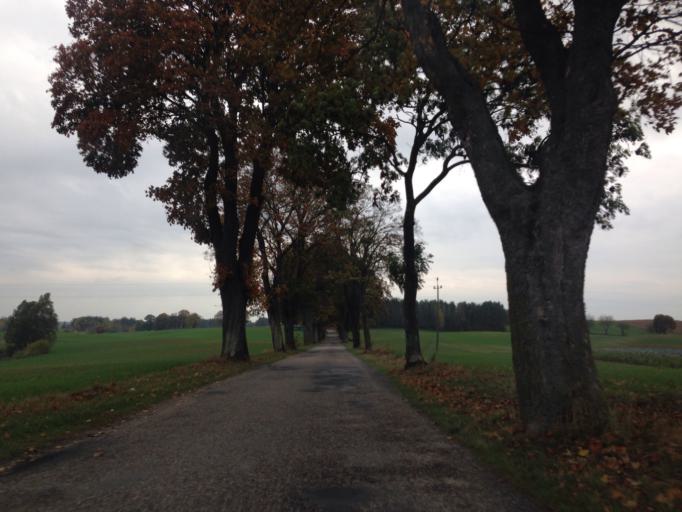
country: PL
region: Kujawsko-Pomorskie
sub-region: Powiat brodnicki
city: Bartniczka
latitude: 53.2821
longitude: 19.6912
